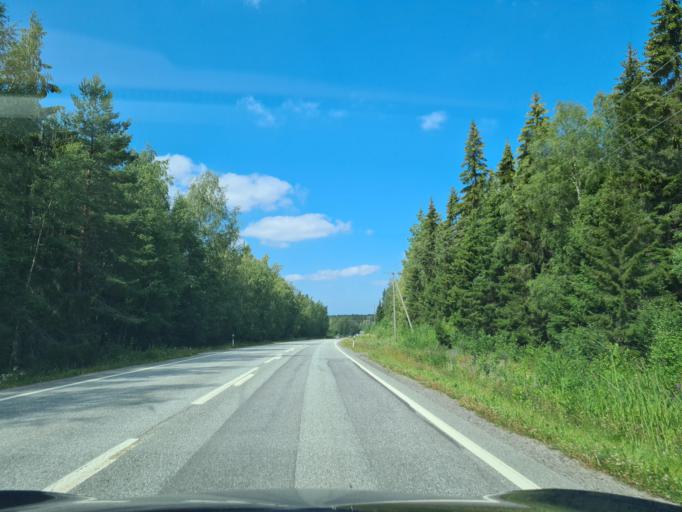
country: FI
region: Ostrobothnia
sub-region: Vaasa
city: Vaasa
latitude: 63.1845
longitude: 21.5678
